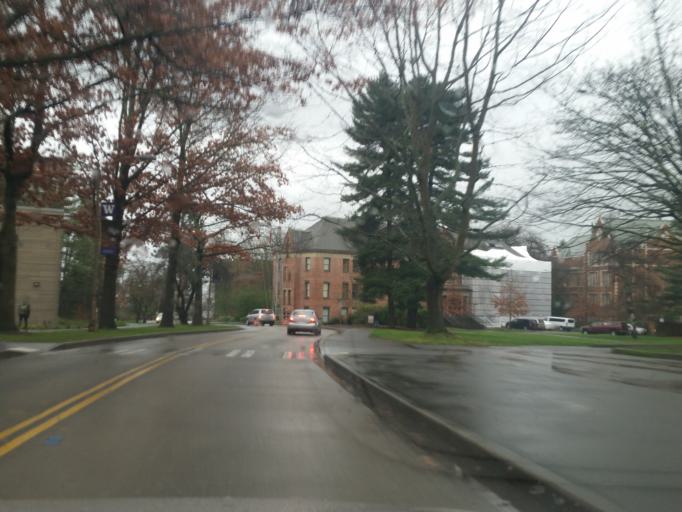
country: US
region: Washington
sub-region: King County
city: Seattle
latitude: 47.6587
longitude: -122.3058
